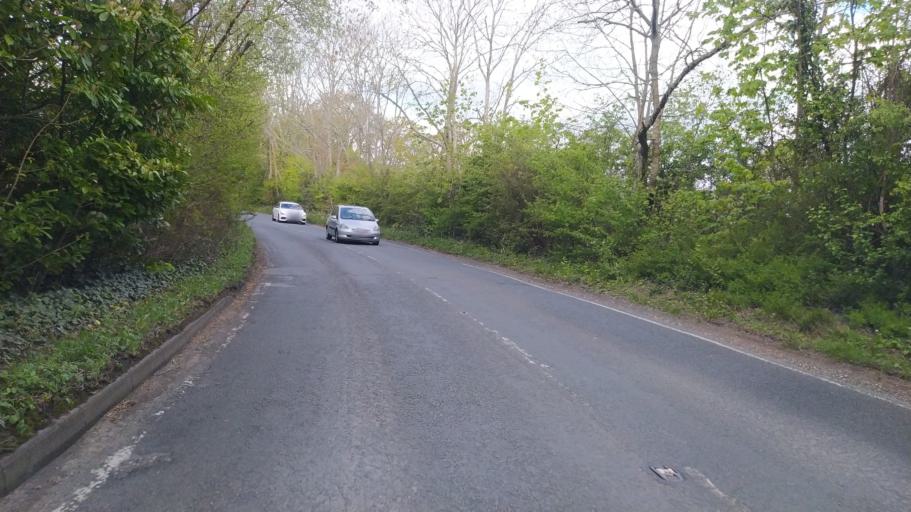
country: GB
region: England
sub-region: Hampshire
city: Marchwood
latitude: 50.8748
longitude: -1.4335
